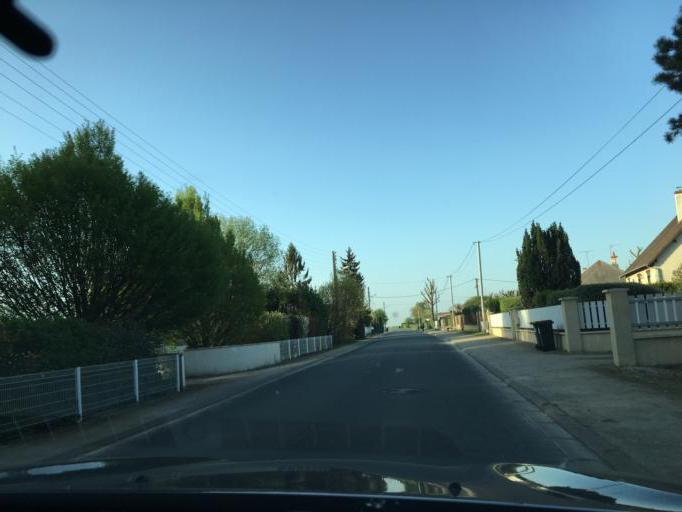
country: FR
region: Centre
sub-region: Departement du Loir-et-Cher
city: Ouzouer-le-Marche
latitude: 47.9142
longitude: 1.5248
